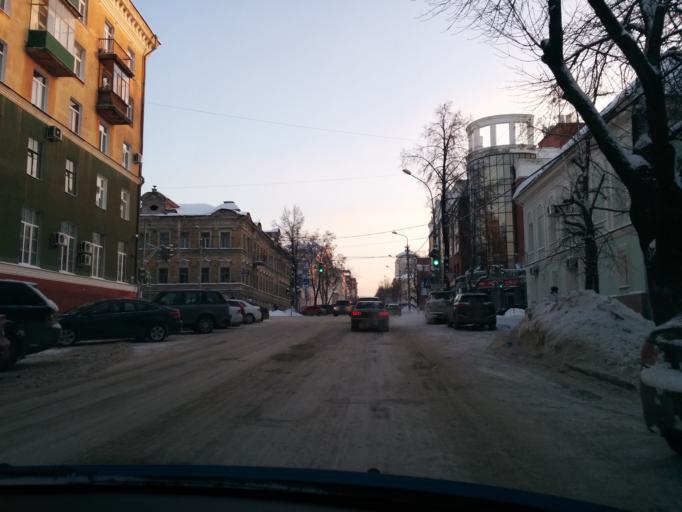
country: RU
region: Perm
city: Perm
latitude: 58.0145
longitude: 56.2414
